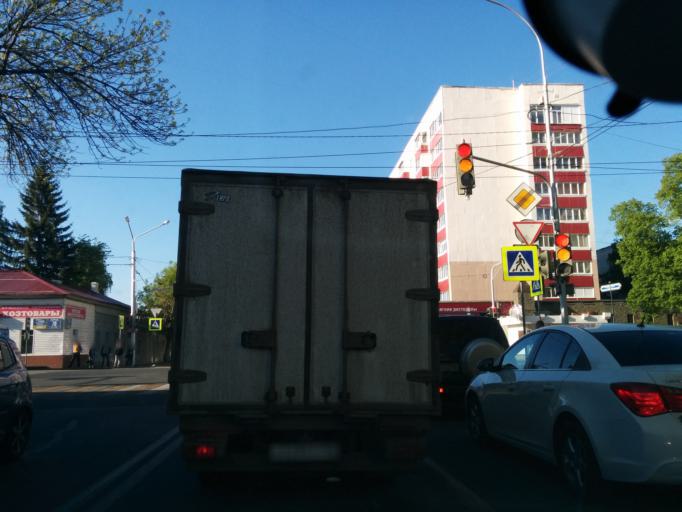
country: RU
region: Bashkortostan
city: Ufa
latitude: 54.7241
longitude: 55.9337
